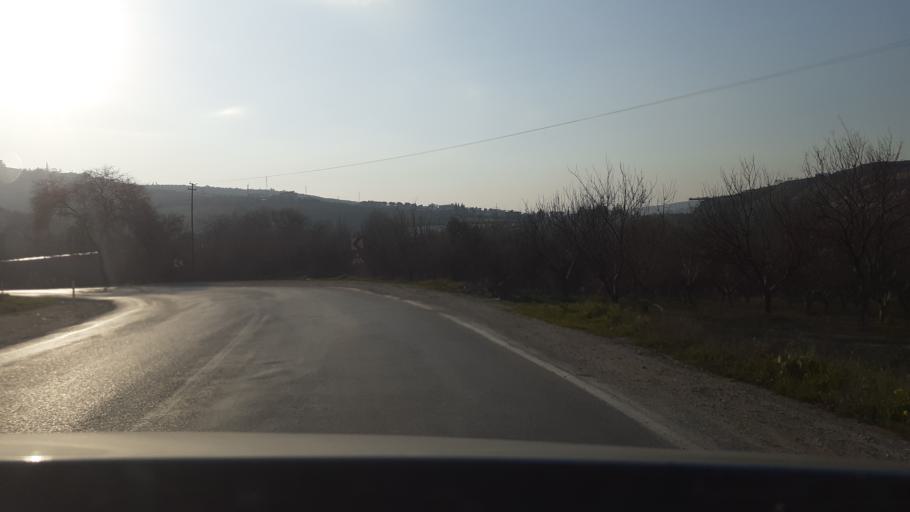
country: TR
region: Hatay
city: Oymakli
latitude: 36.1107
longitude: 36.2759
